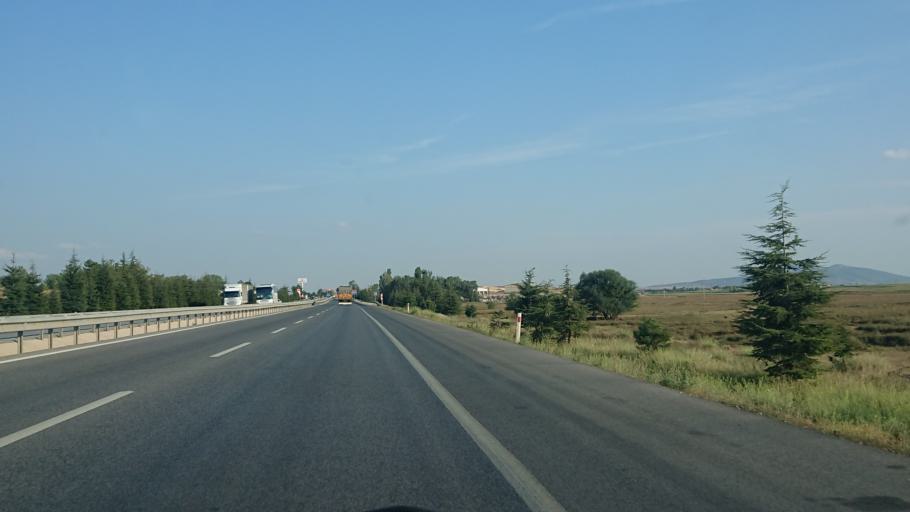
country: TR
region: Eskisehir
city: Sevinc
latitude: 39.6450
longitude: 30.7946
